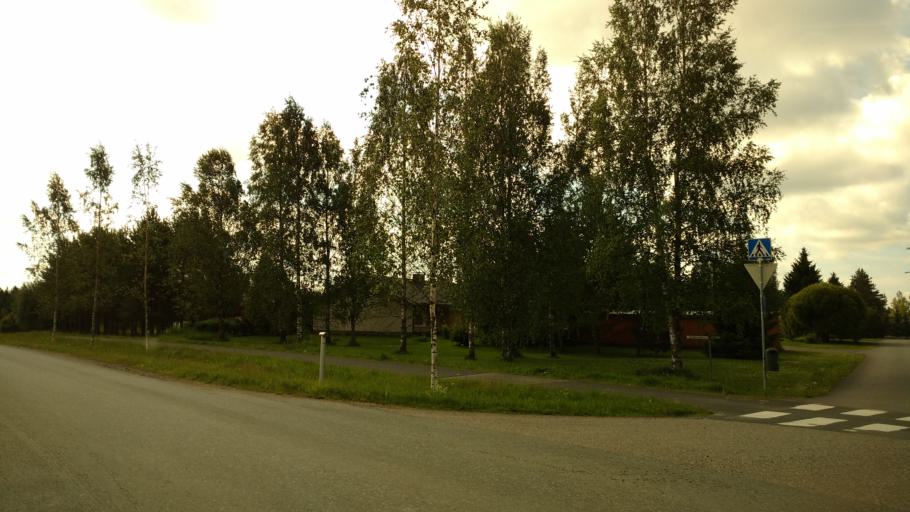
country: FI
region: Haeme
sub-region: Forssa
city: Ypaejae
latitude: 60.8066
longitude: 23.2762
